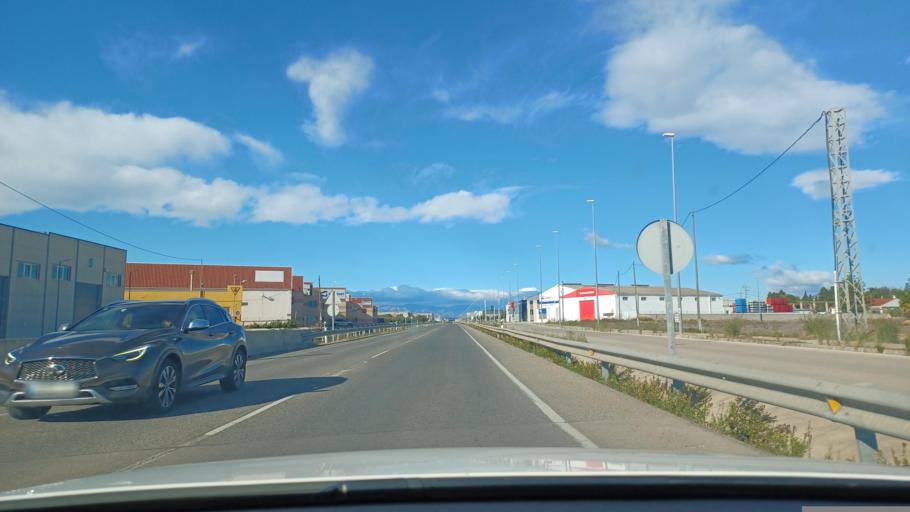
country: ES
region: Valencia
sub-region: Provincia de Castello
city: Vinaros
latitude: 40.4832
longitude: 0.4721
